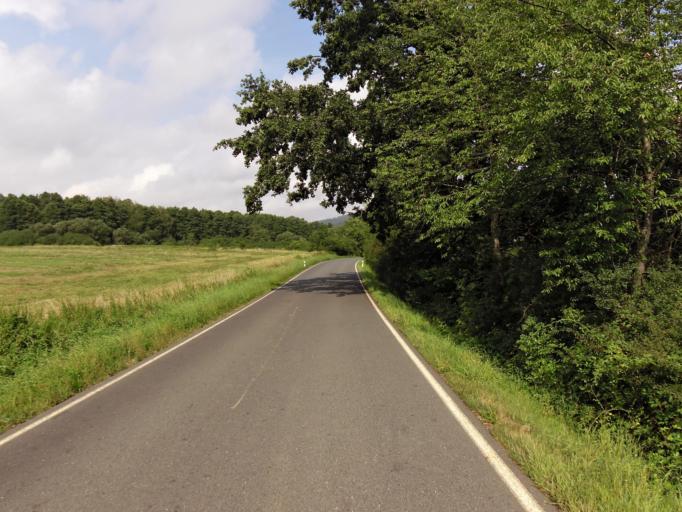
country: CZ
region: Central Bohemia
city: Tynec nad Sazavou
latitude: 49.8648
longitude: 14.5837
